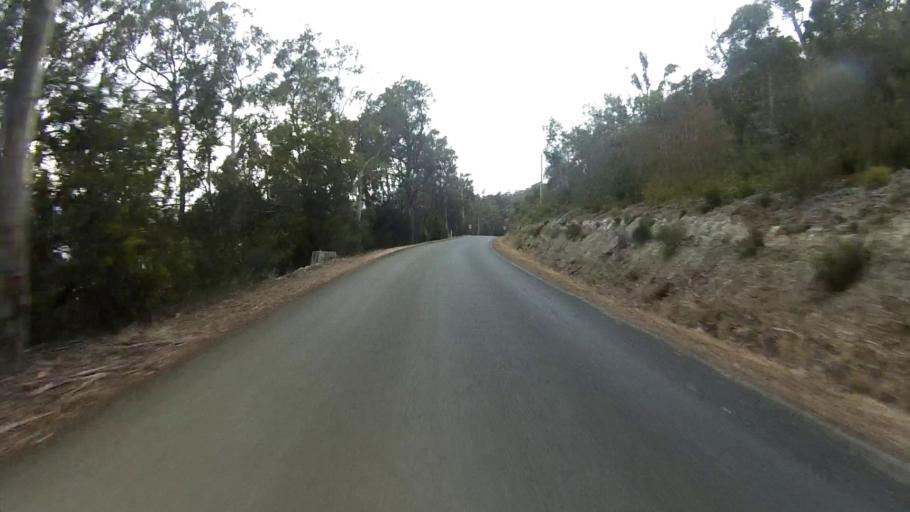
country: AU
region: Tasmania
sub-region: Huon Valley
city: Cygnet
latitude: -43.2180
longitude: 147.0940
